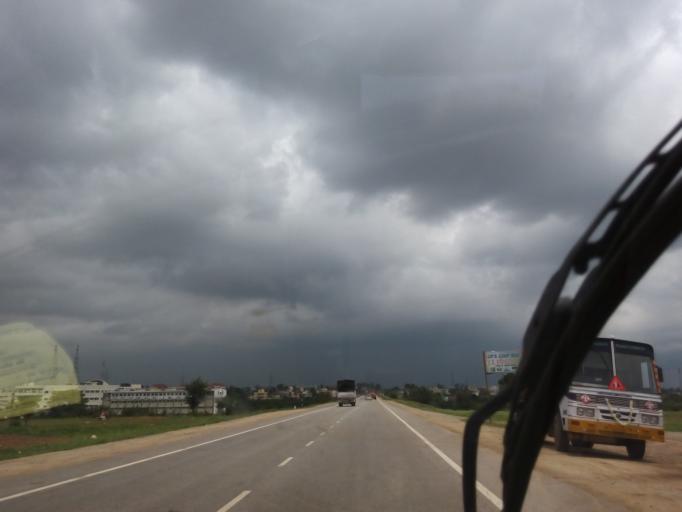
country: IN
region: Karnataka
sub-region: Hassan
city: Hassan
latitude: 12.9937
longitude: 76.1177
